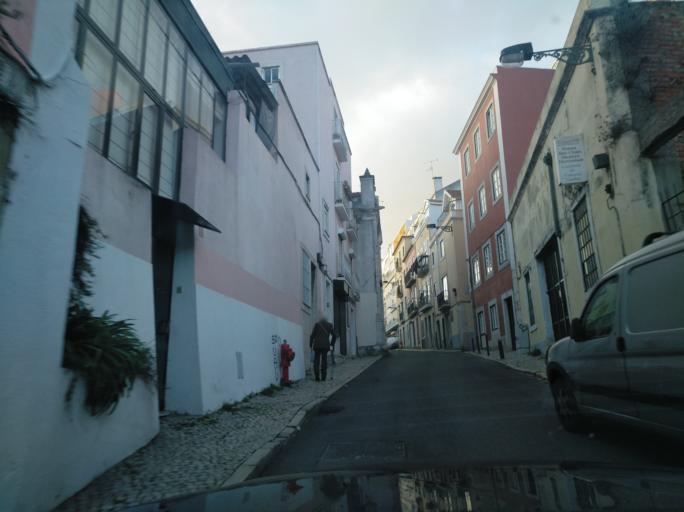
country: PT
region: Lisbon
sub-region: Lisbon
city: Lisbon
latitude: 38.7163
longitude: -9.1257
